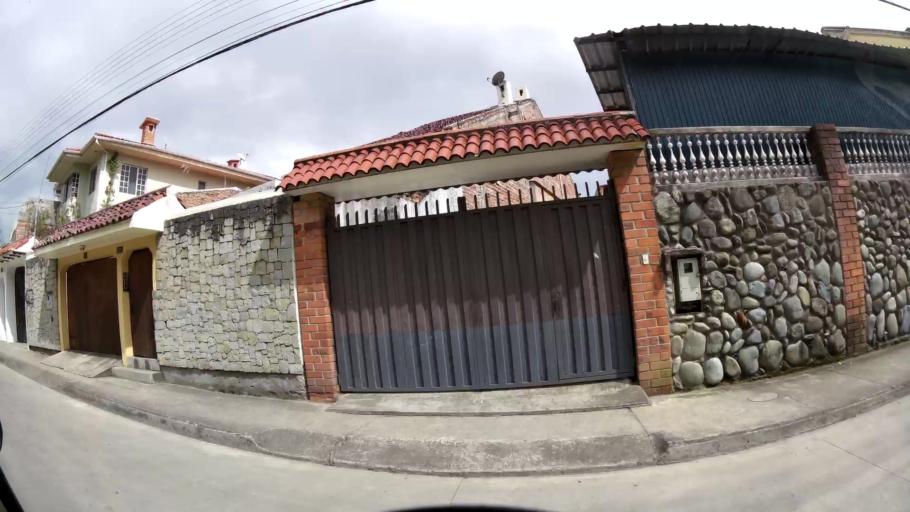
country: EC
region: Azuay
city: Cuenca
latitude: -2.9171
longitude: -79.0106
